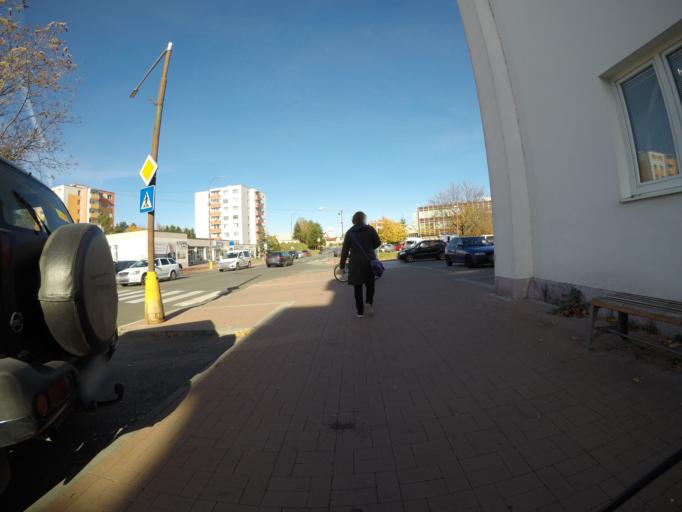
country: SK
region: Trenciansky
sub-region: Okres Nove Mesto nad Vahom
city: Nove Mesto nad Vahom
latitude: 48.7537
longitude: 17.8304
